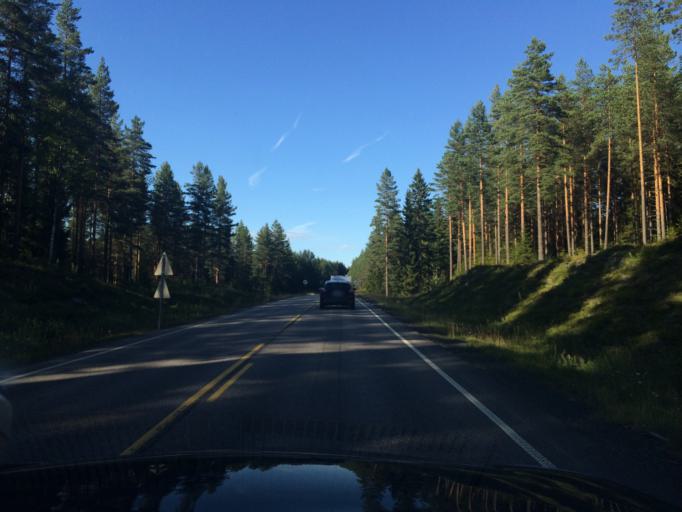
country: NO
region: Hedmark
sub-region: Elverum
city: Elverum
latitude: 60.9608
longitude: 11.7106
